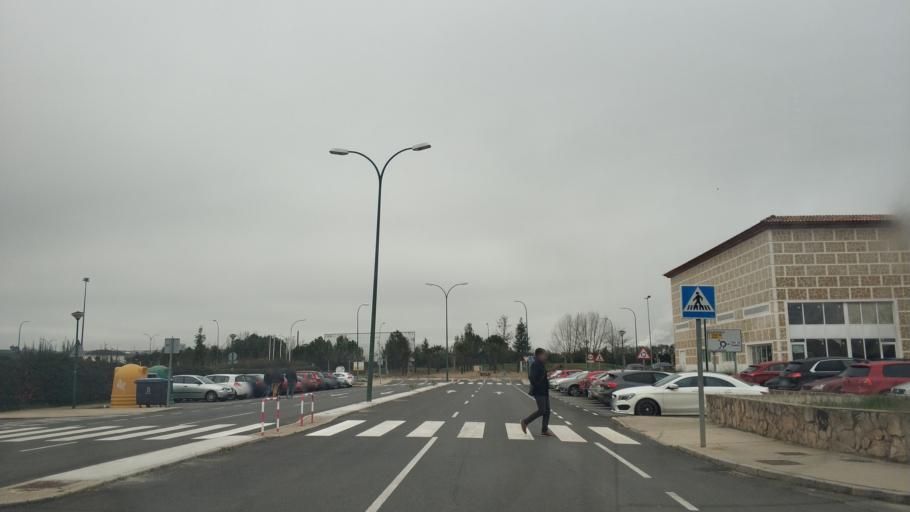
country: ES
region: Castille and Leon
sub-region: Provincia de Salamanca
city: Villamayor
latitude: 40.9953
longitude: -5.7224
